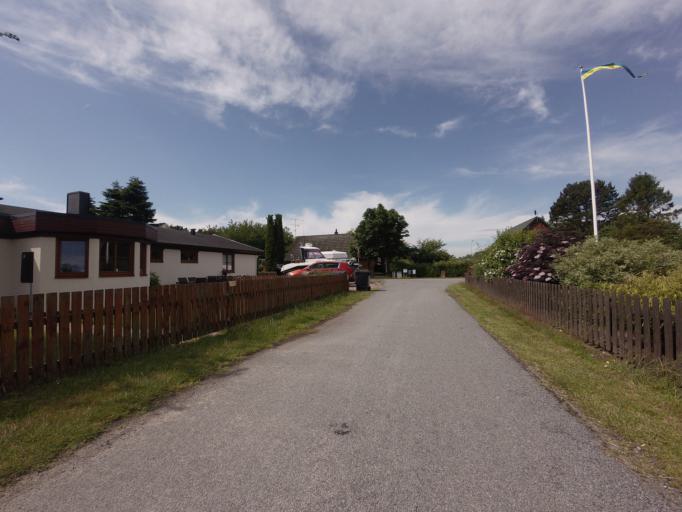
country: SE
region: Skane
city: Smygehamn
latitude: 55.3575
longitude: 13.4185
